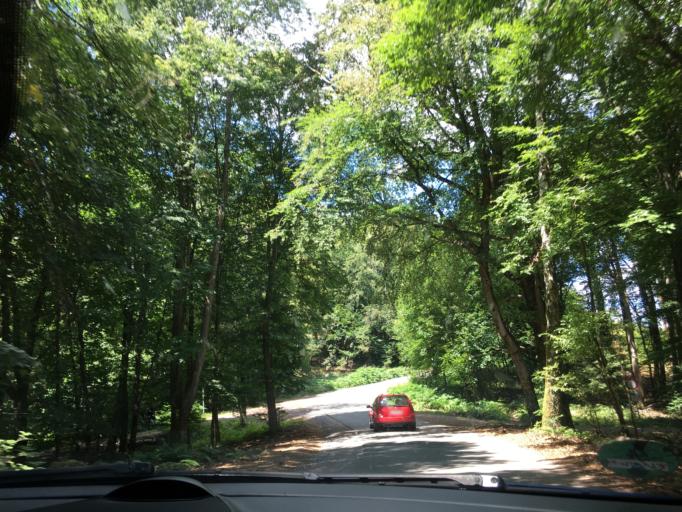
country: DE
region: Rheinland-Pfalz
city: Hauenstein
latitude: 49.2455
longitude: 7.8278
